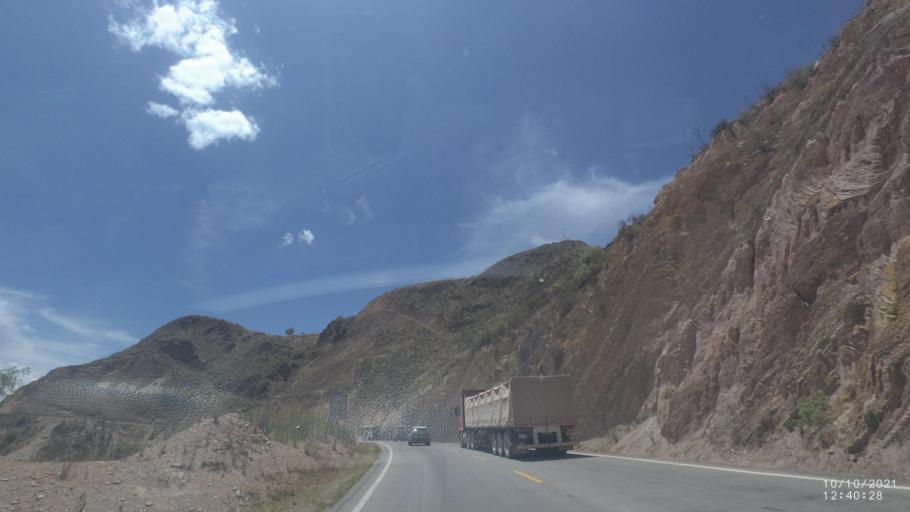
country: BO
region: Cochabamba
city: Irpa Irpa
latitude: -17.6407
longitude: -66.3886
